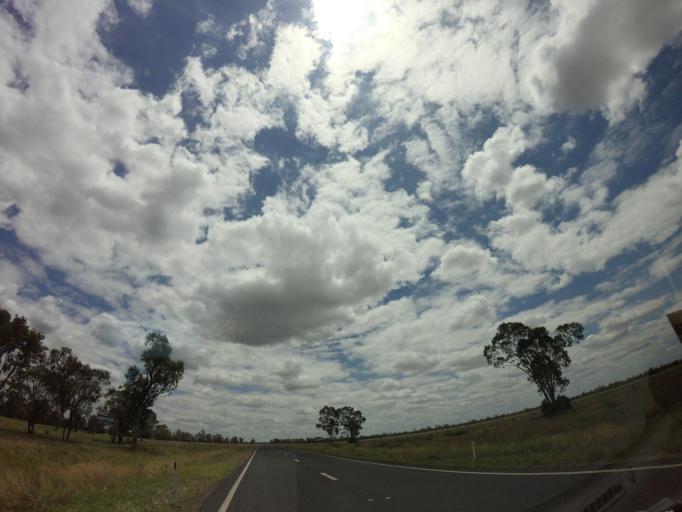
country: AU
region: New South Wales
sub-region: Moree Plains
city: Boggabilla
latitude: -28.6355
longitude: 150.3442
